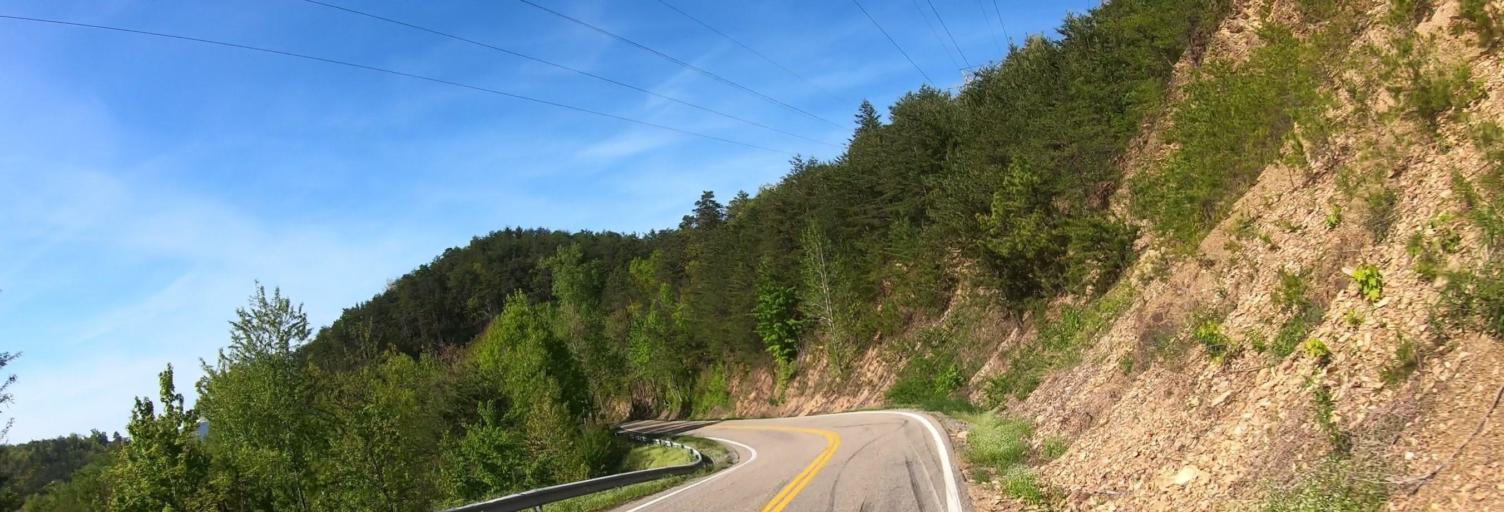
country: US
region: Tennessee
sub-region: Loudon County
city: Greenback
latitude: 35.5085
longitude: -83.9854
